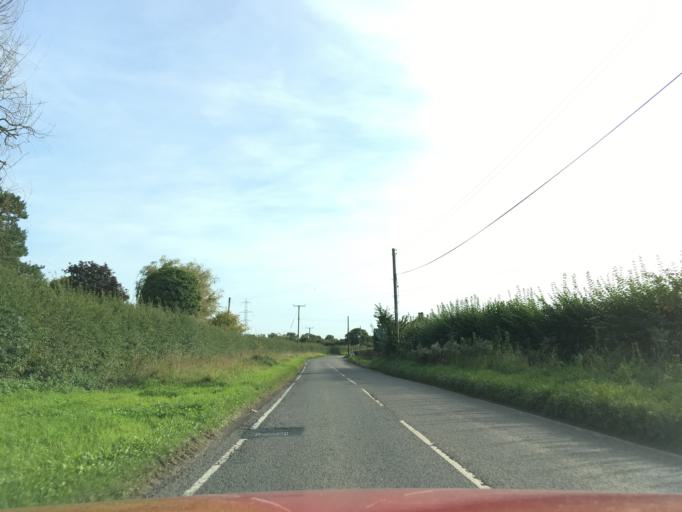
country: GB
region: England
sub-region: South Gloucestershire
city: Winterbourne
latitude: 51.5498
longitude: -2.5128
